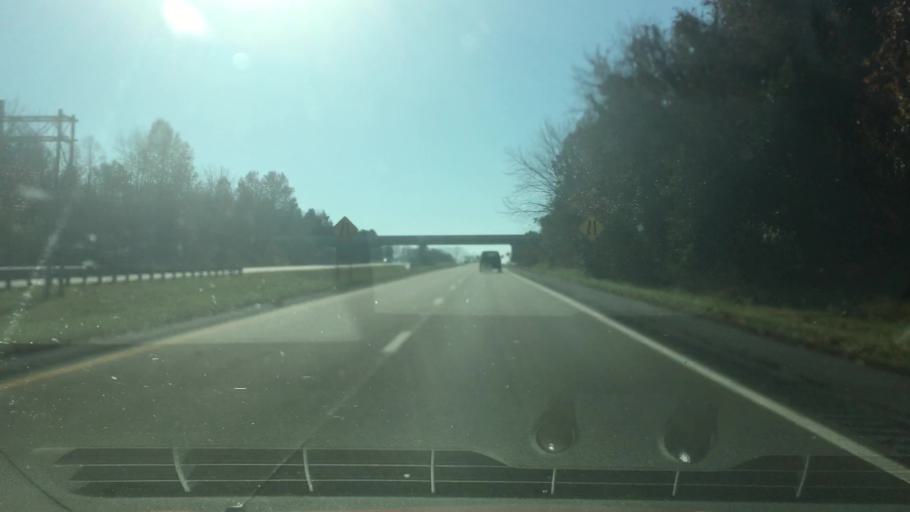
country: US
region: Ohio
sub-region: Wayne County
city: Wooster
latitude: 40.7778
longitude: -81.9144
